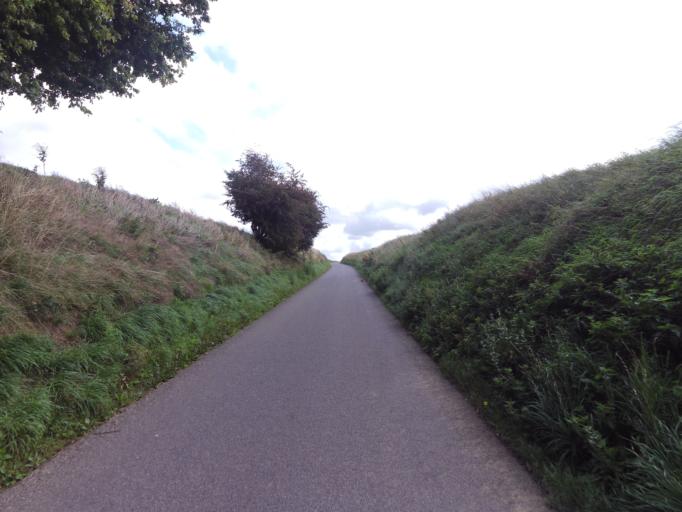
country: BE
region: Wallonia
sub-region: Province de Liege
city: Villers-le-Bouillet
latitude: 50.6167
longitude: 5.2155
